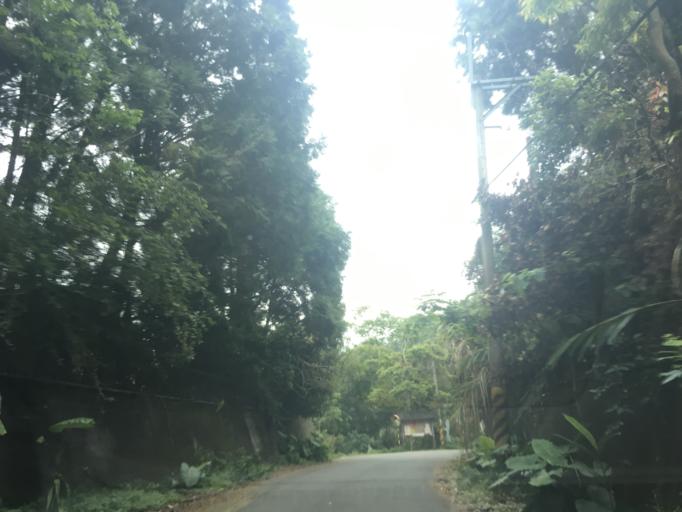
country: TW
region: Taiwan
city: Zhongxing New Village
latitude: 24.0483
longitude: 120.7892
